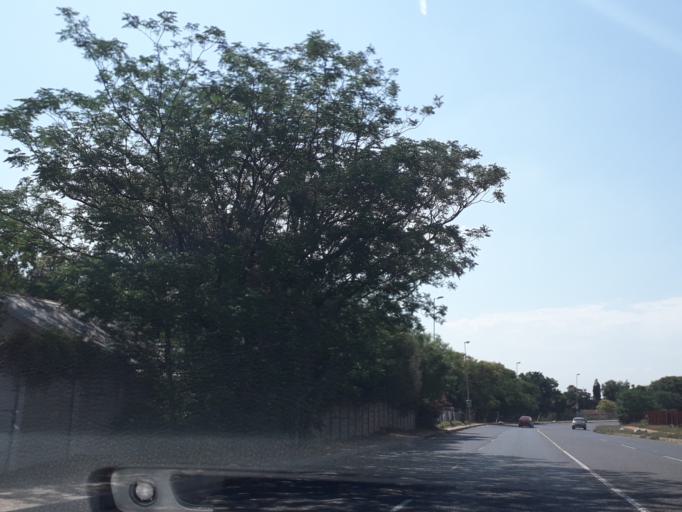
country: ZA
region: Gauteng
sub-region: City of Johannesburg Metropolitan Municipality
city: Johannesburg
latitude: -26.0801
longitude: 27.9970
